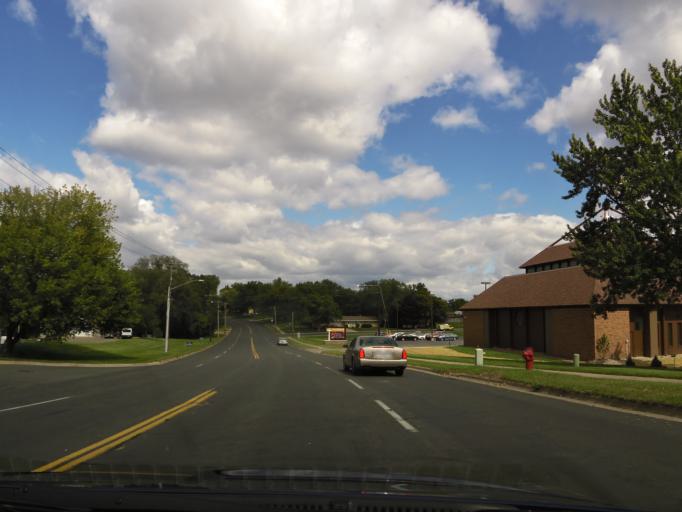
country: US
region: Minnesota
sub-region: Dakota County
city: Inver Grove Heights
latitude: 44.8394
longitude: -93.0414
